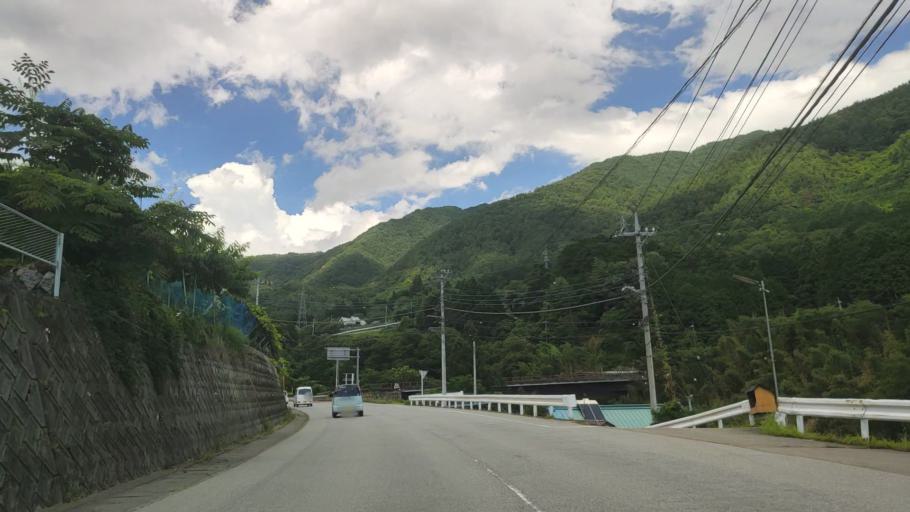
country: JP
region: Yamanashi
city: Enzan
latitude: 35.7651
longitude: 138.7355
